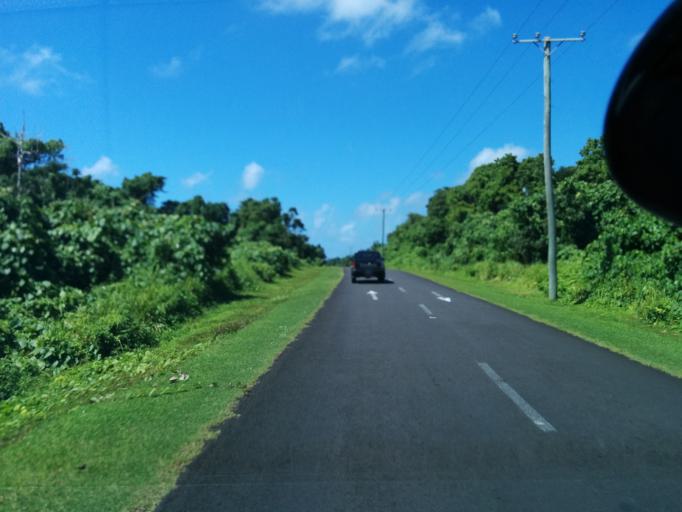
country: WS
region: Fa`asaleleaga
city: Safotulafai
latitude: -13.5332
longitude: -172.2548
